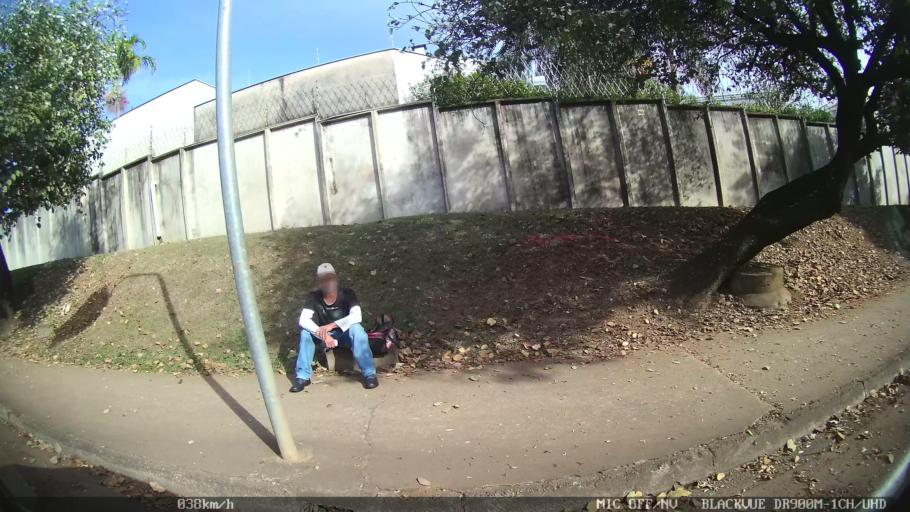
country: BR
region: Sao Paulo
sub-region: Piracicaba
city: Piracicaba
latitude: -22.7297
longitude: -47.6727
